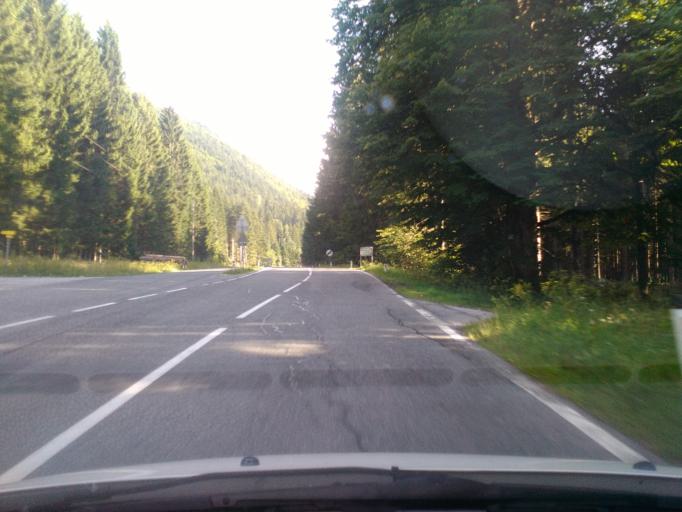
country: AT
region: Carinthia
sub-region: Politischer Bezirk Villach Land
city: Arnoldstein
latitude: 46.5240
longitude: 13.7514
